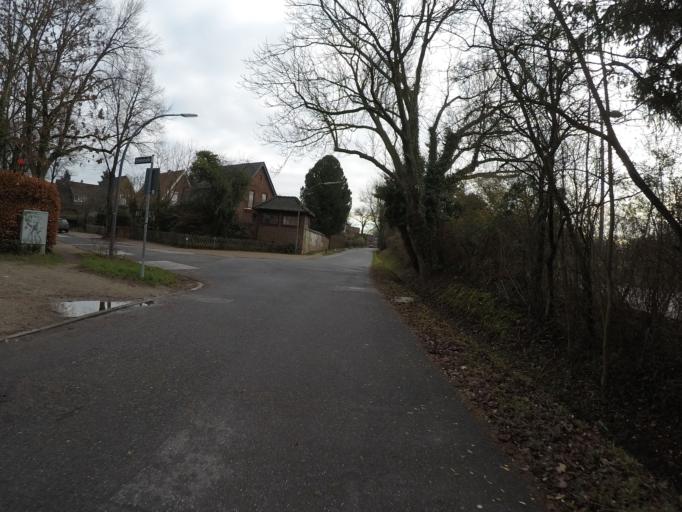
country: DE
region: Hamburg
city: Stellingen
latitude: 53.5978
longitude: 9.9537
